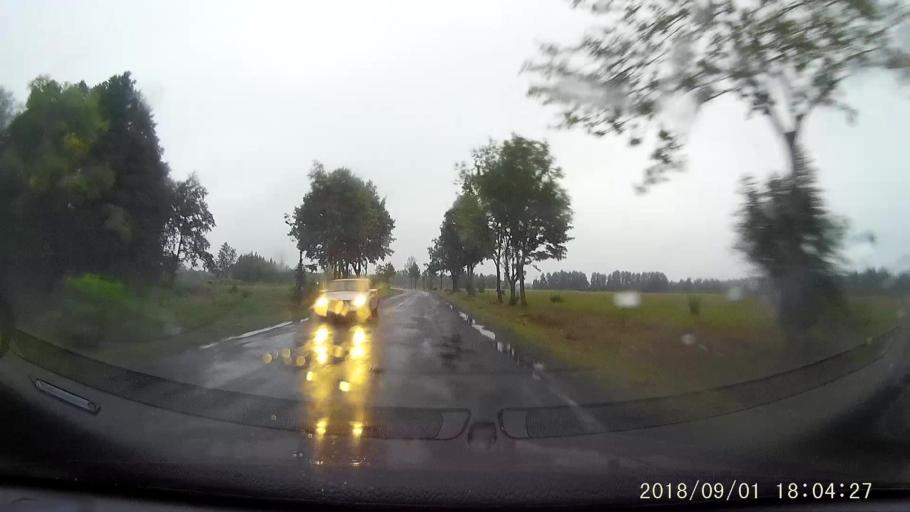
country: PL
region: Lubusz
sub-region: Powiat zaganski
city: Gozdnica
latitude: 51.3708
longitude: 15.1651
